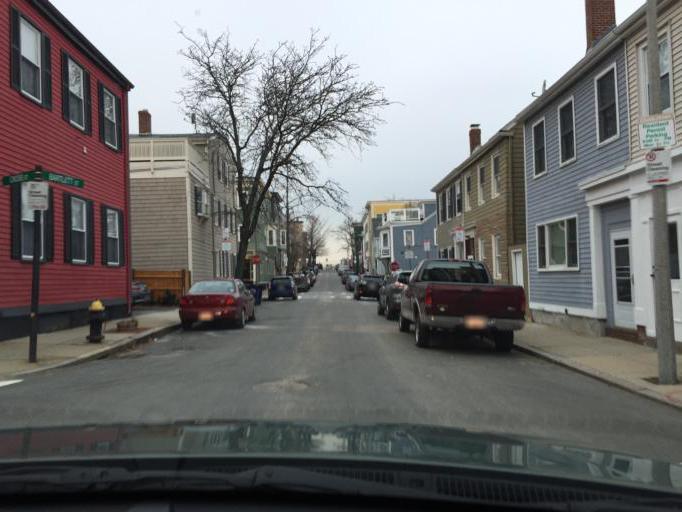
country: US
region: Massachusetts
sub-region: Suffolk County
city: Boston
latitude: 42.3775
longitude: -71.0620
